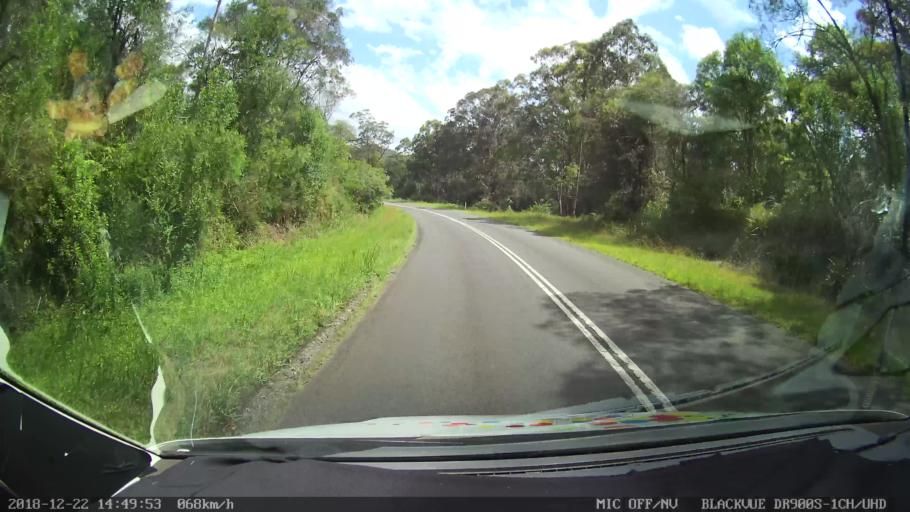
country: AU
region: New South Wales
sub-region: Bellingen
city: Dorrigo
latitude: -30.1907
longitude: 152.5424
